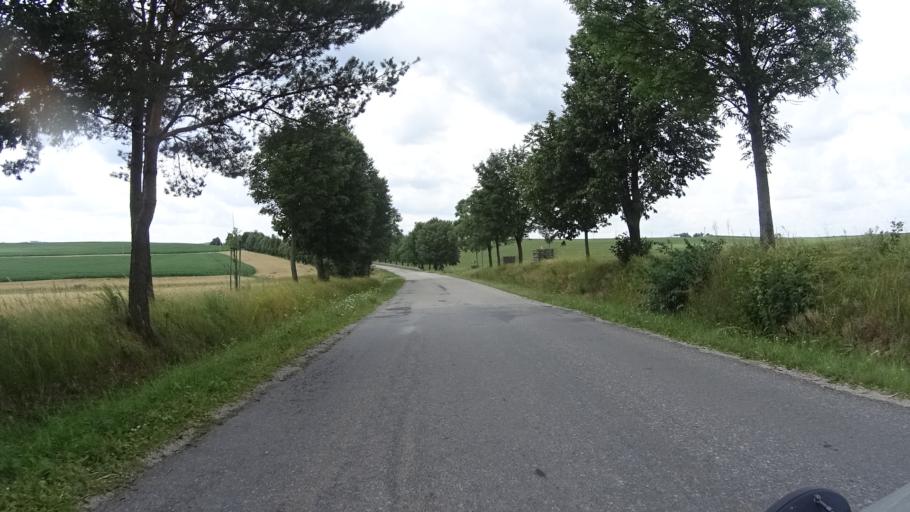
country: CZ
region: Vysocina
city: Merin
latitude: 49.3983
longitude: 15.9040
